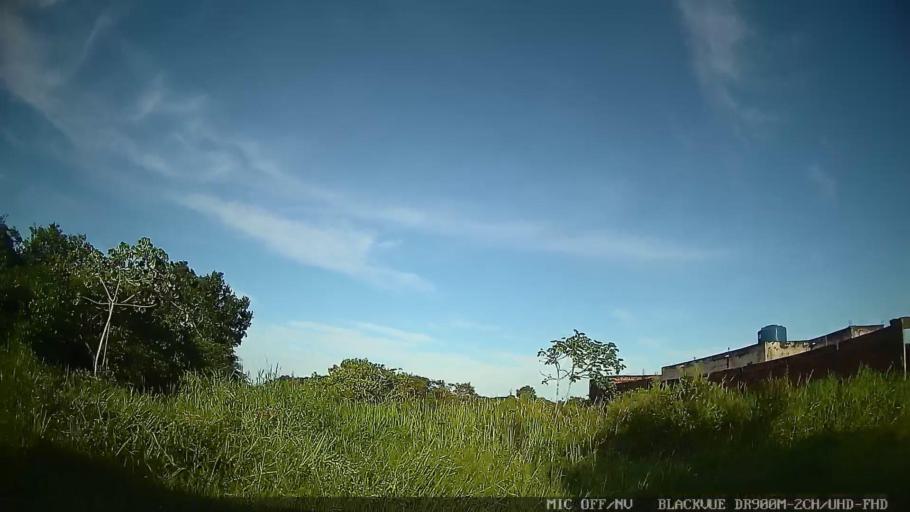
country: BR
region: Sao Paulo
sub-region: Iguape
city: Iguape
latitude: -24.7519
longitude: -47.5669
